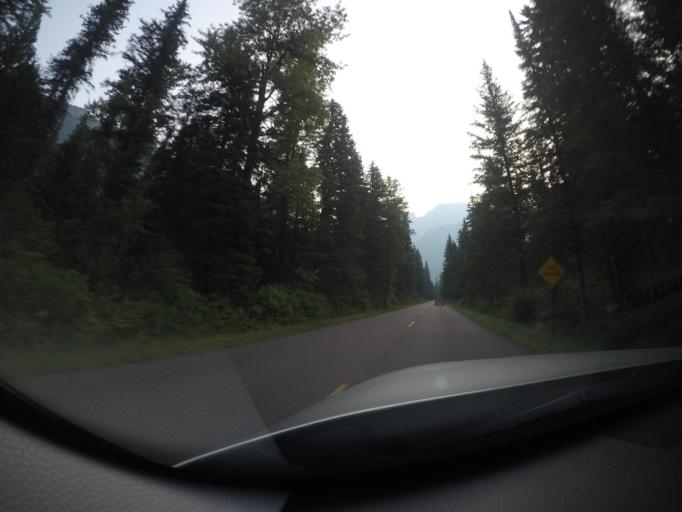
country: US
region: Montana
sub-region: Flathead County
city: Columbia Falls
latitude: 48.7162
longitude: -113.7785
